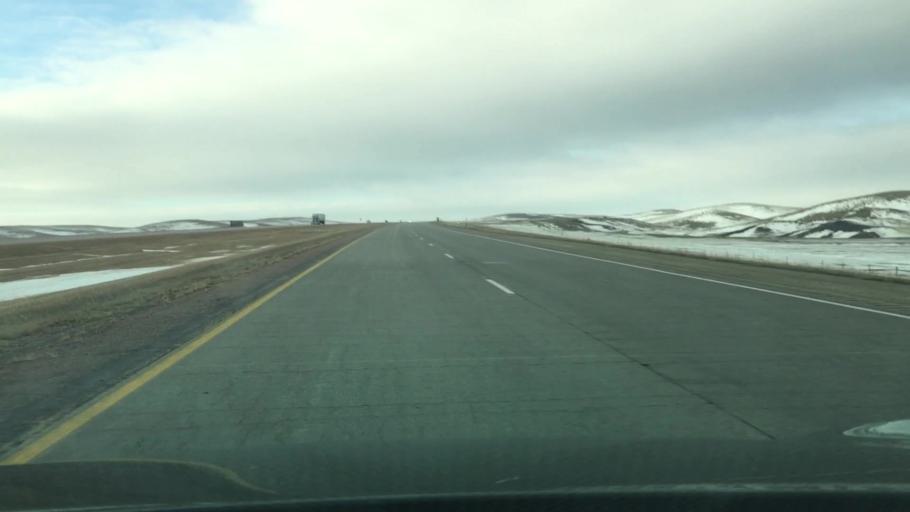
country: US
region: South Dakota
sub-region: Brule County
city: Chamberlain
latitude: 43.8273
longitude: -99.4561
